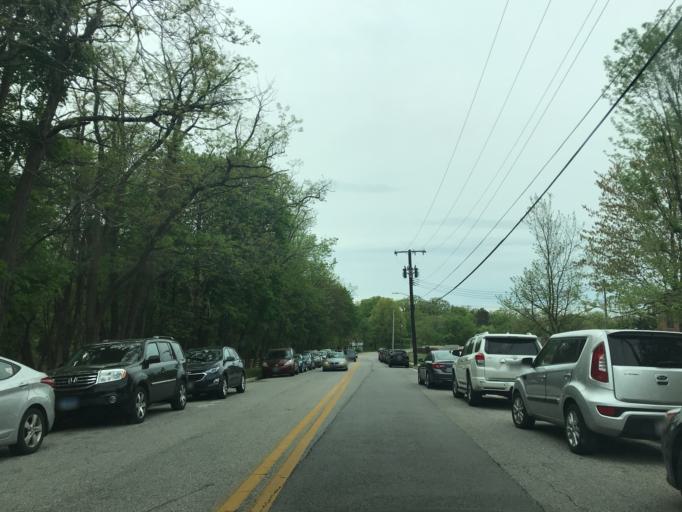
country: US
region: Maryland
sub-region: Baltimore County
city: Catonsville
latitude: 39.2665
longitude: -76.7318
